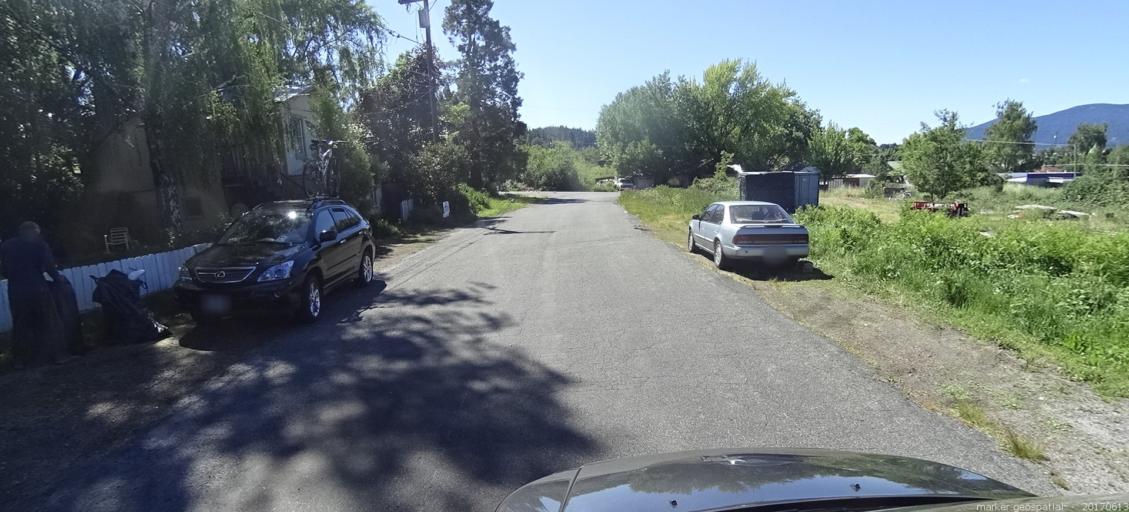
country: US
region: California
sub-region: Siskiyou County
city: Mount Shasta
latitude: 41.3178
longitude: -122.3149
